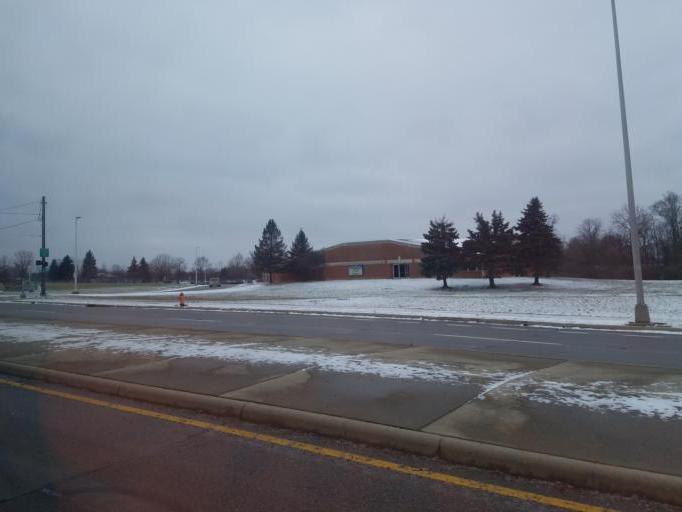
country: US
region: Ohio
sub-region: Franklin County
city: Worthington
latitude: 40.1169
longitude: -83.0540
